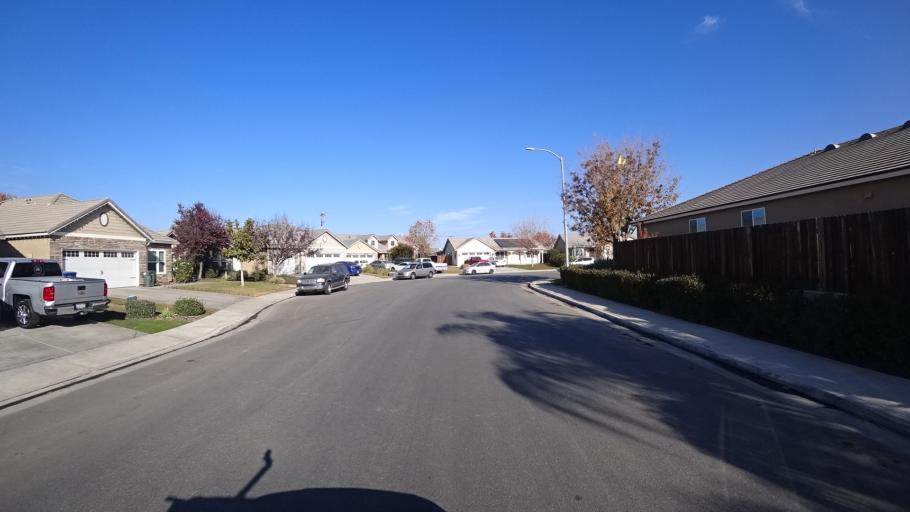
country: US
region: California
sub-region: Kern County
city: Greenfield
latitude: 35.2733
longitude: -119.0649
